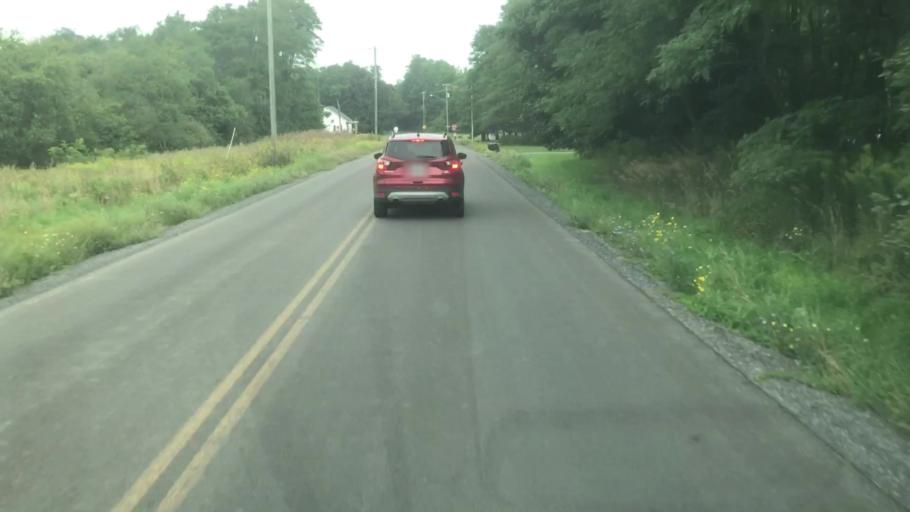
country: US
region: New York
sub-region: Cayuga County
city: Melrose Park
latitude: 42.9199
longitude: -76.4894
